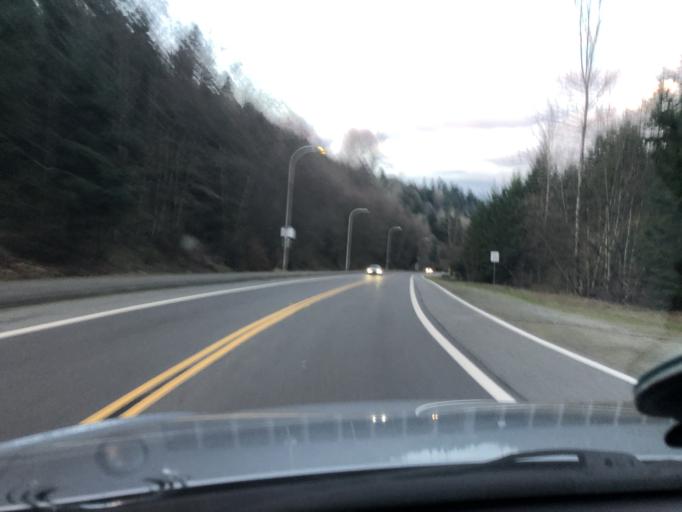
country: US
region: Washington
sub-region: King County
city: Lakeland North
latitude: 47.3184
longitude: -122.2562
